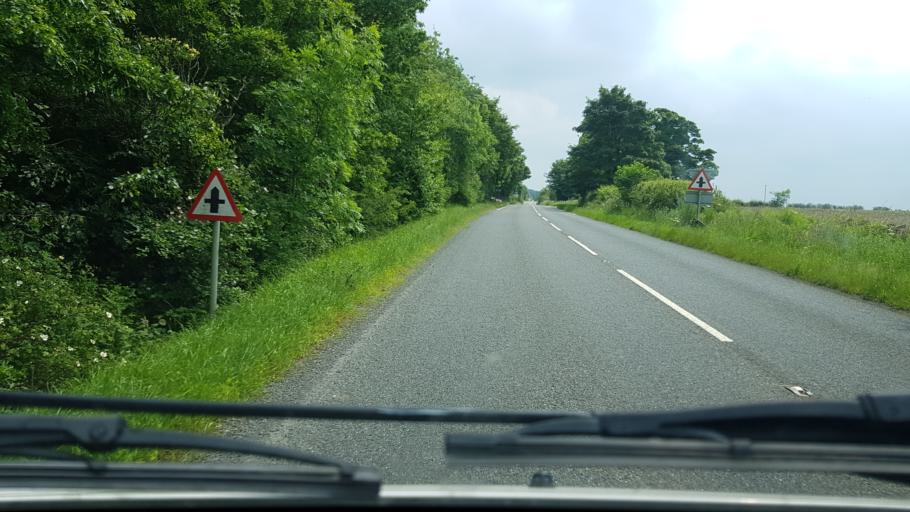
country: GB
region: England
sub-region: Gloucestershire
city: Chipping Campden
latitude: 51.9959
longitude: -1.7814
